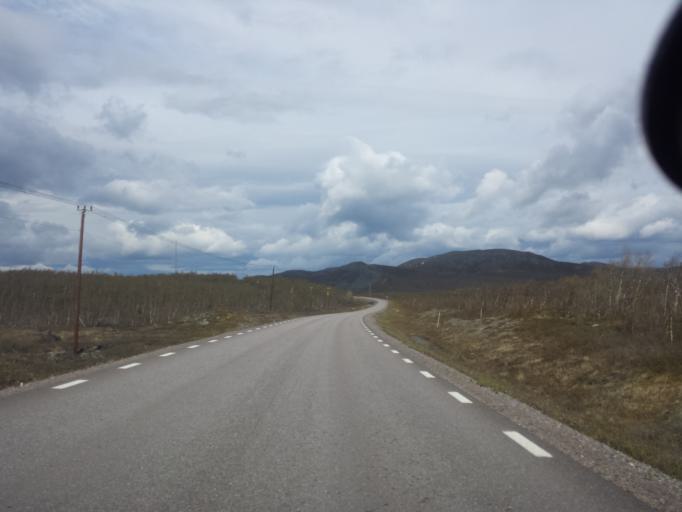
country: SE
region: Norrbotten
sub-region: Kiruna Kommun
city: Kiruna
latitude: 68.1672
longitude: 19.7889
